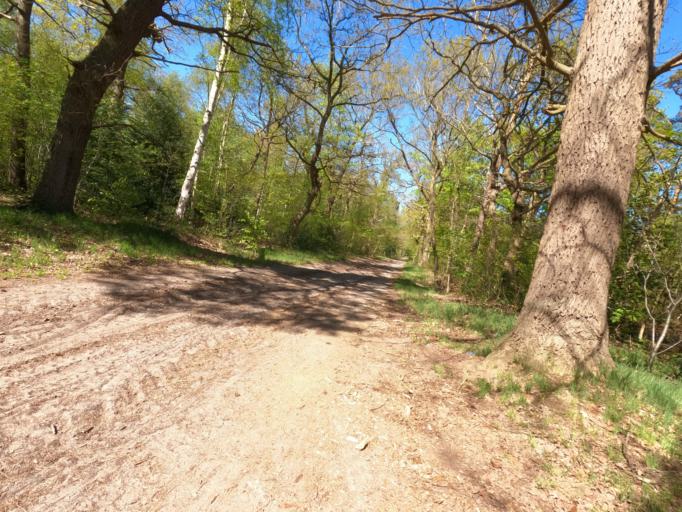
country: DE
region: Mecklenburg-Vorpommern
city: Born
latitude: 54.3876
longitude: 12.5219
